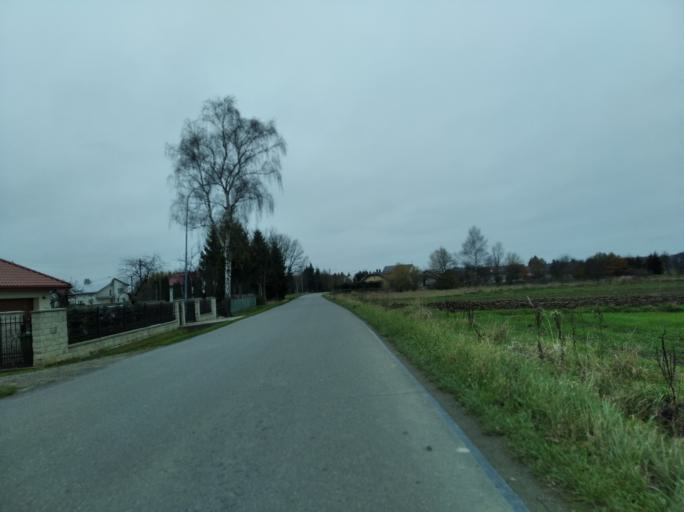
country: PL
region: Subcarpathian Voivodeship
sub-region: Powiat krosnienski
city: Chorkowka
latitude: 49.6829
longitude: 21.6749
